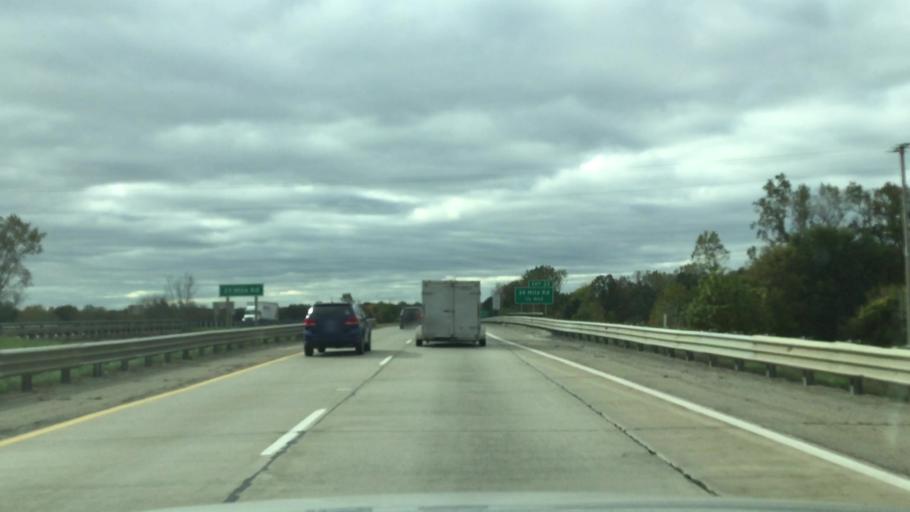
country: US
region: Michigan
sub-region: Macomb County
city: Shelby
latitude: 42.7289
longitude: -83.0268
